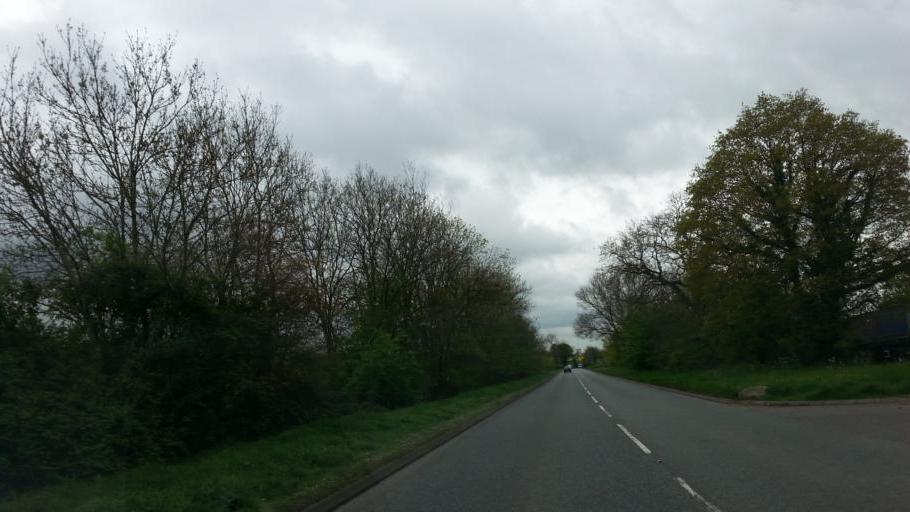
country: GB
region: England
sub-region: Leicestershire
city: Lutterworth
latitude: 52.4308
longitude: -1.2156
